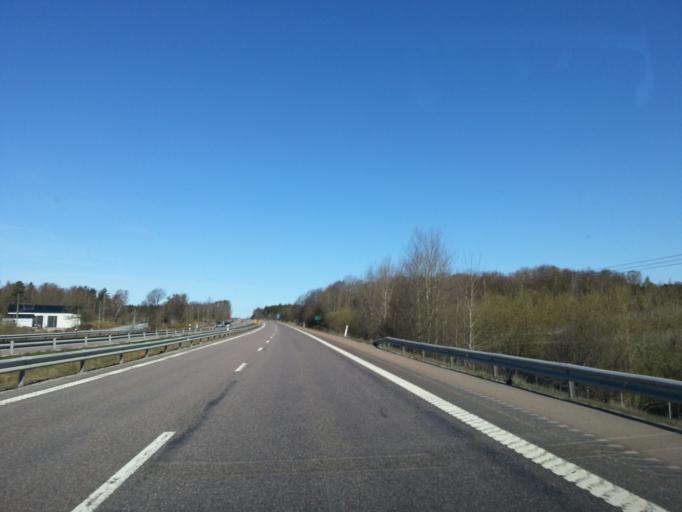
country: SE
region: Vaestra Goetaland
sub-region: Kungalvs Kommun
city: Kode
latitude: 57.9349
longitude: 11.8697
